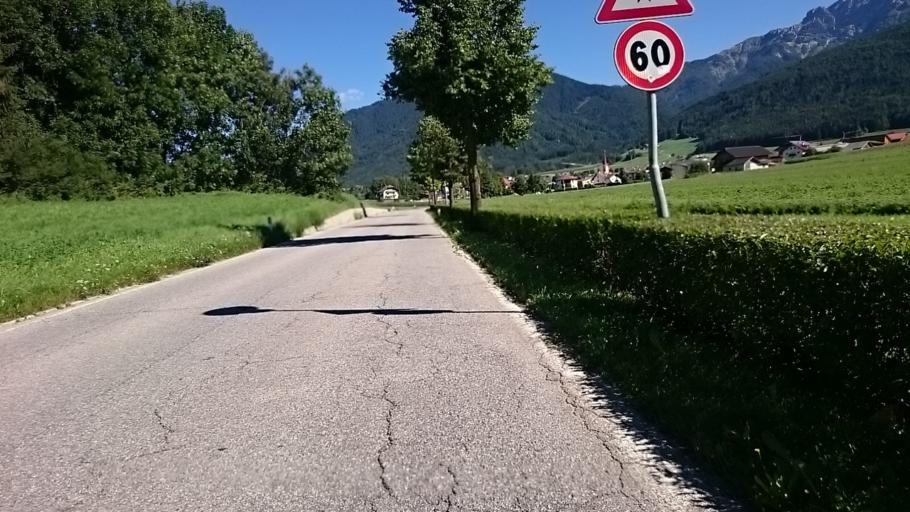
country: IT
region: Trentino-Alto Adige
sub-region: Bolzano
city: Valdaora di Mezzo
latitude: 46.7663
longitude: 12.0235
